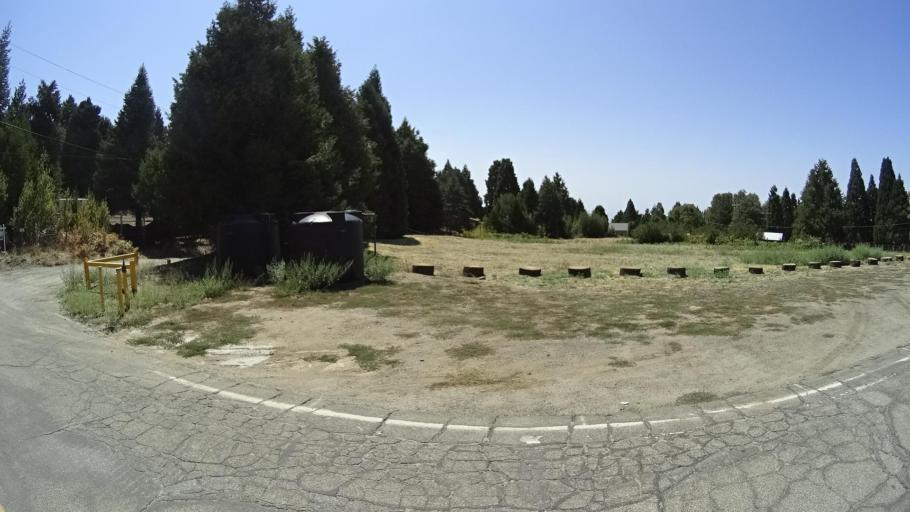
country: US
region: California
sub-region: Riverside County
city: Aguanga
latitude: 33.3102
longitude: -116.8494
